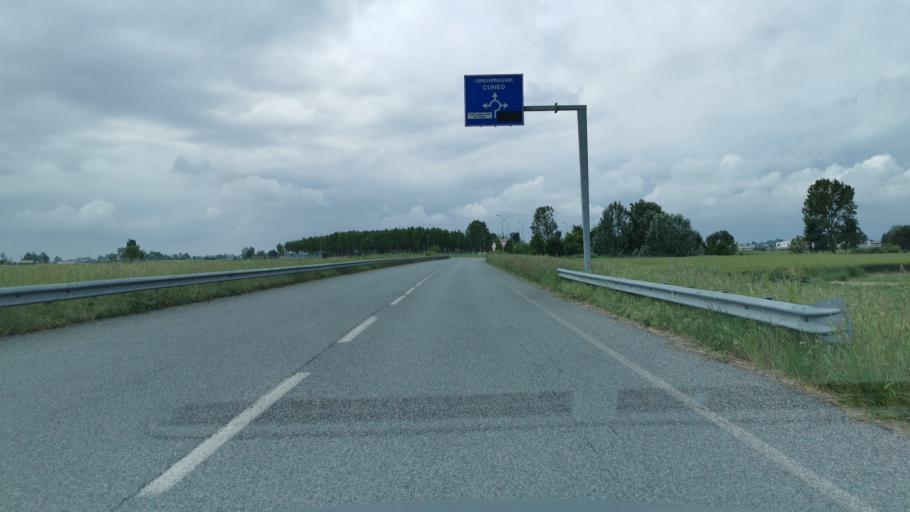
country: IT
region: Piedmont
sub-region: Provincia di Cuneo
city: Racconigi
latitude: 44.7510
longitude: 7.6921
